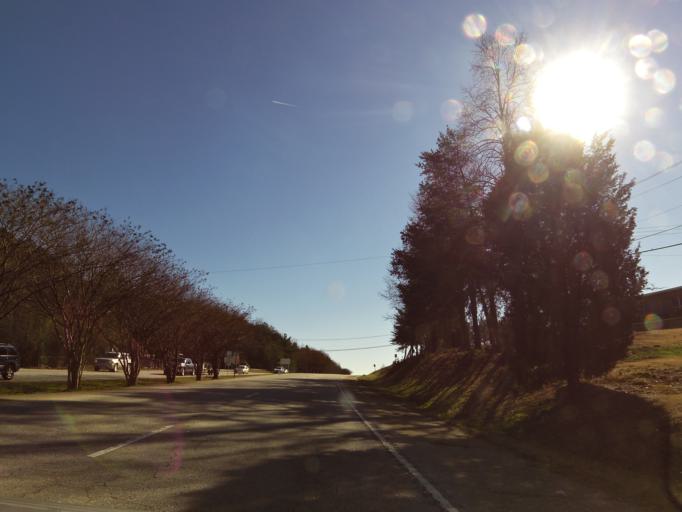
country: US
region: South Carolina
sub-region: Greenville County
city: Travelers Rest
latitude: 34.9440
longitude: -82.4364
